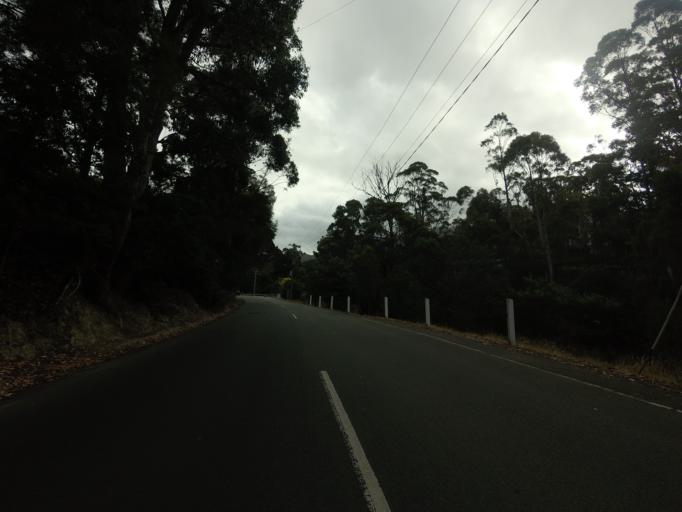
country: AU
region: Tasmania
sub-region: Hobart
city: Dynnyrne
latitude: -42.9026
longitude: 147.2778
